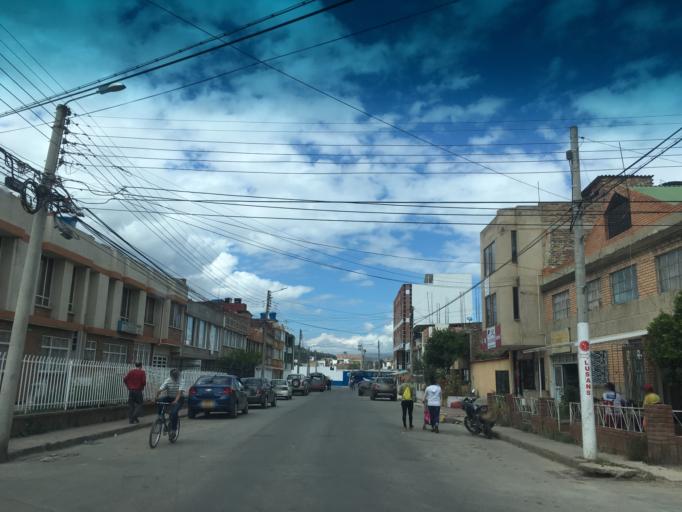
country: CO
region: Boyaca
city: Sogamoso
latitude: 5.7176
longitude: -72.9356
